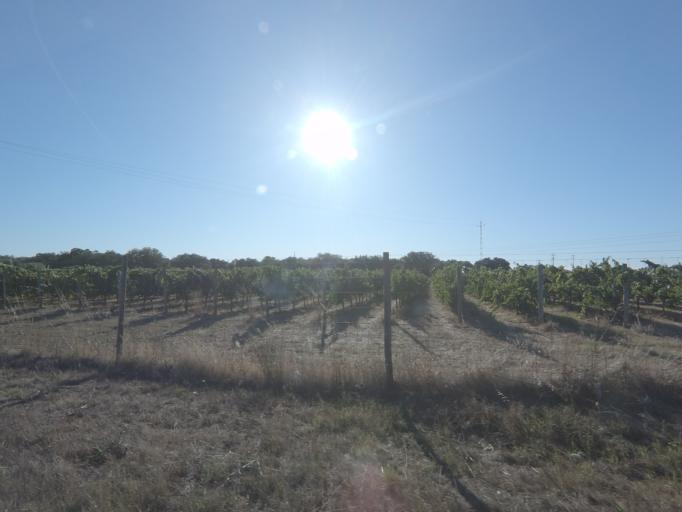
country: PT
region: Setubal
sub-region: Palmela
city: Quinta do Anjo
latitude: 38.5434
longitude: -8.9847
